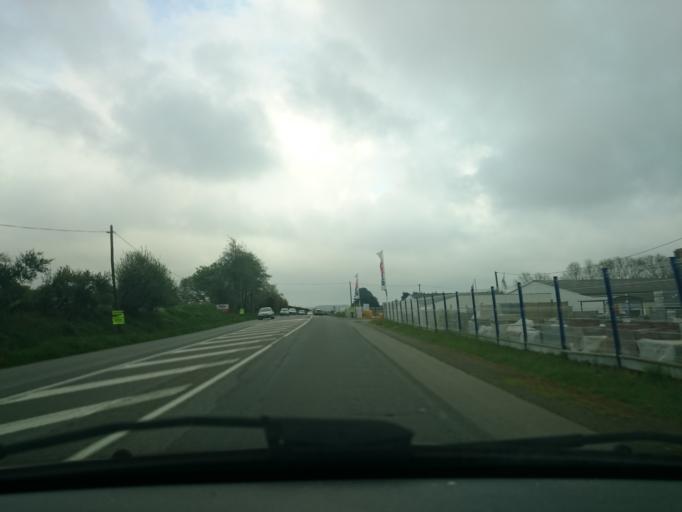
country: FR
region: Brittany
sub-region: Departement du Finistere
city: Saint-Renan
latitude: 48.4499
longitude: -4.6234
